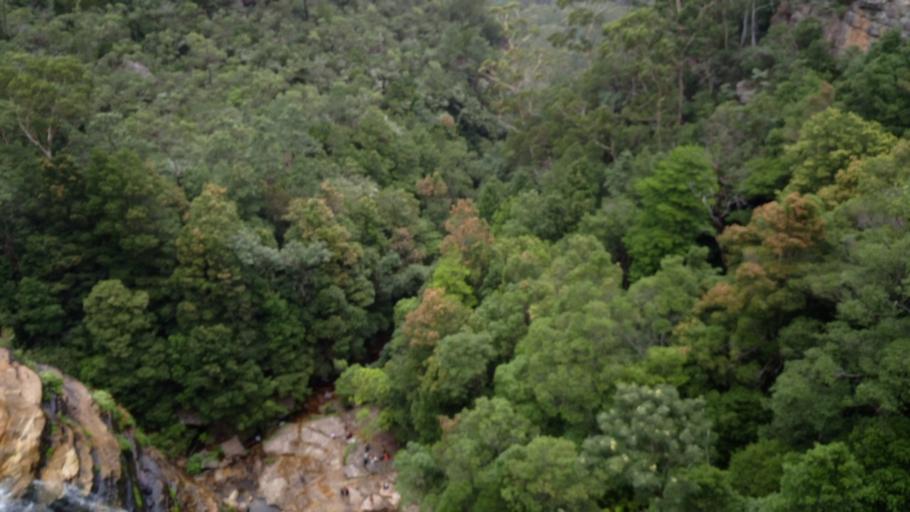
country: AU
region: New South Wales
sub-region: Blue Mountains Municipality
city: Leura
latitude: -33.7215
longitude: 150.3221
